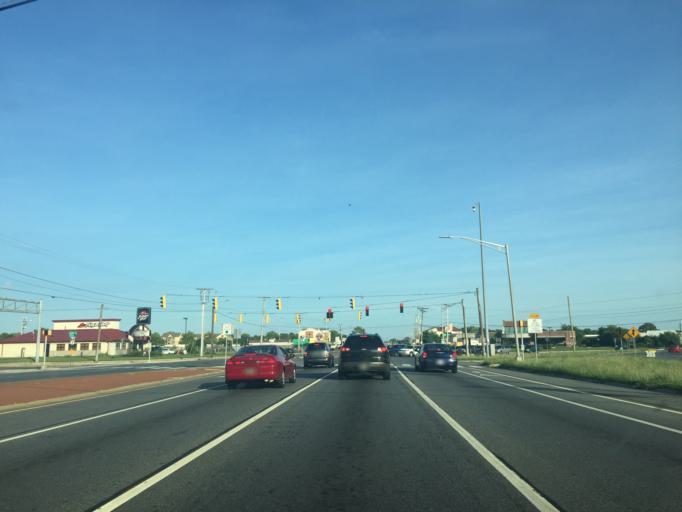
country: US
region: Delaware
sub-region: Kent County
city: Dover
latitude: 39.1816
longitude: -75.5303
